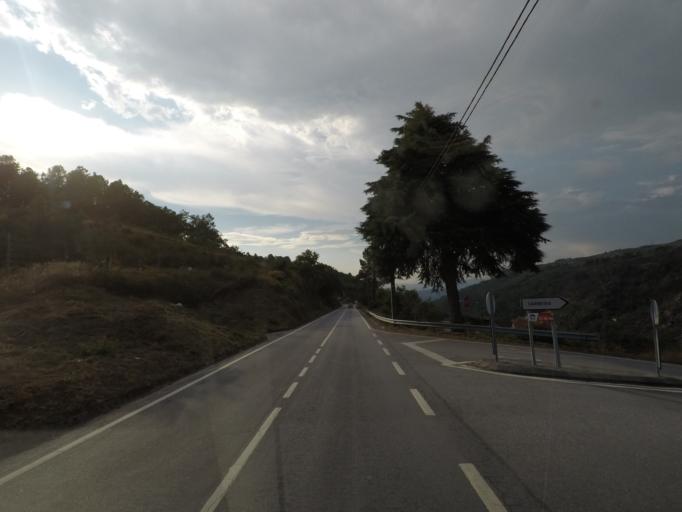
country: PT
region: Porto
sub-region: Baiao
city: Valadares
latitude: 41.2145
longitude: -7.9788
